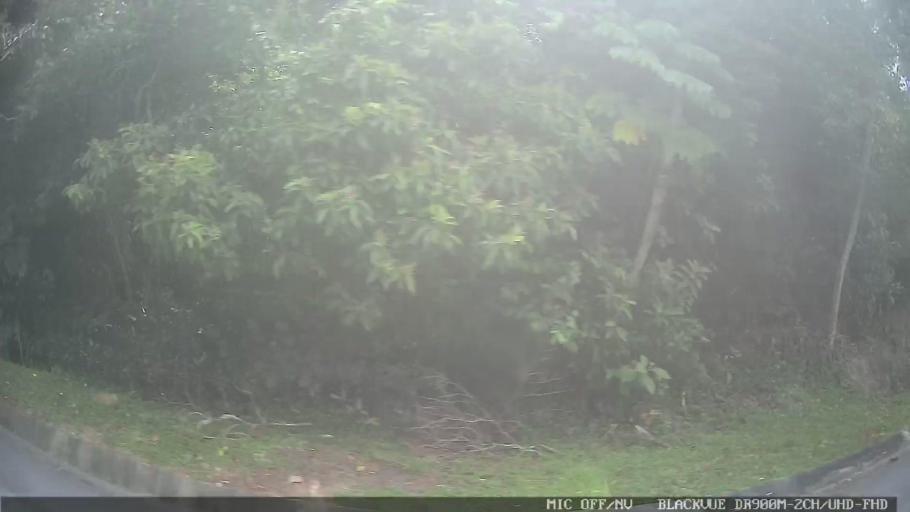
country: BR
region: Sao Paulo
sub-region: Caraguatatuba
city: Caraguatatuba
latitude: -23.5991
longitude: -45.4304
